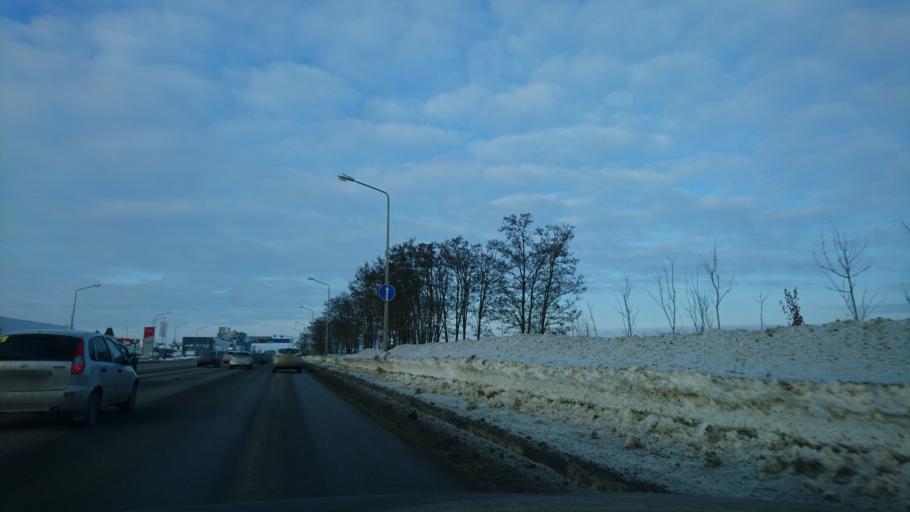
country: RU
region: Belgorod
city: Severnyy
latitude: 50.6503
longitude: 36.5669
